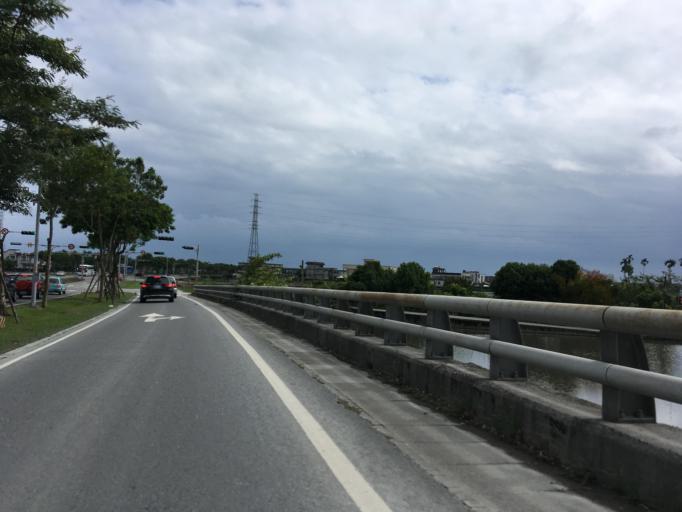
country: TW
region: Taiwan
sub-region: Yilan
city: Yilan
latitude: 24.6779
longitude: 121.7846
